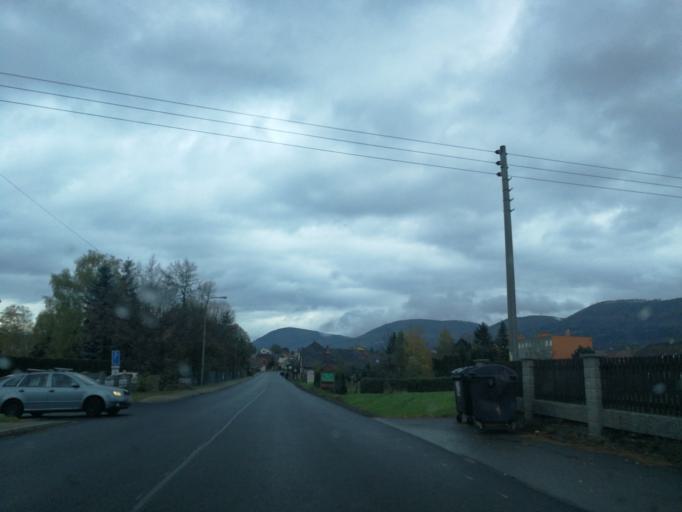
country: CZ
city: Morkov
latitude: 49.5378
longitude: 18.0554
